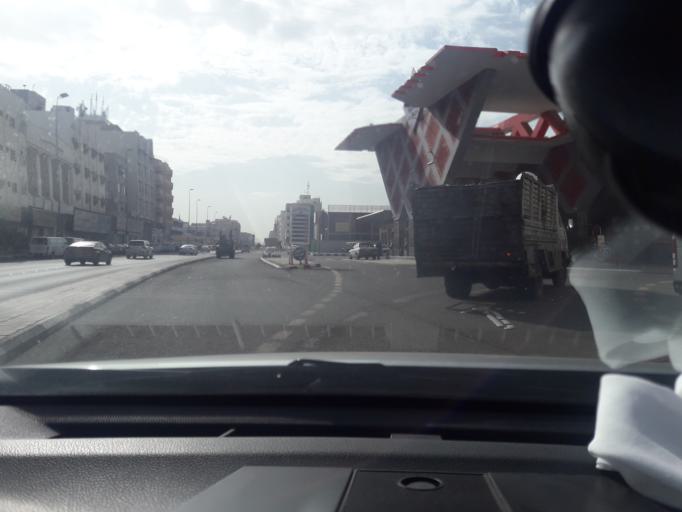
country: SA
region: Al Madinah al Munawwarah
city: Medina
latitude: 24.4537
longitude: 39.6192
